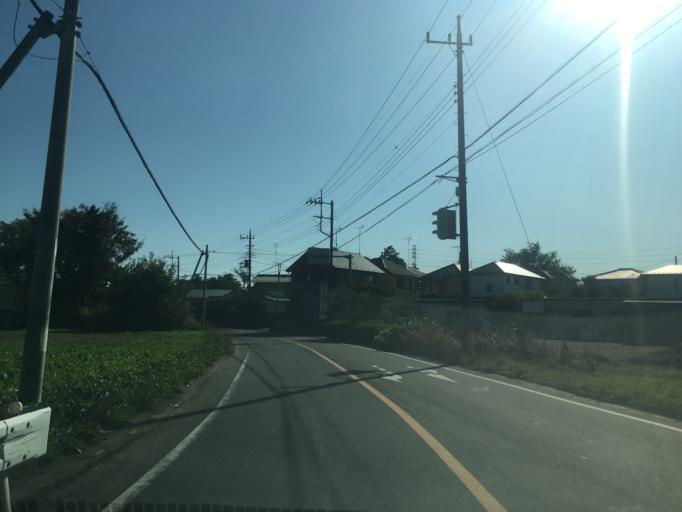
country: JP
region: Saitama
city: Sakado
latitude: 35.9613
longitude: 139.4454
